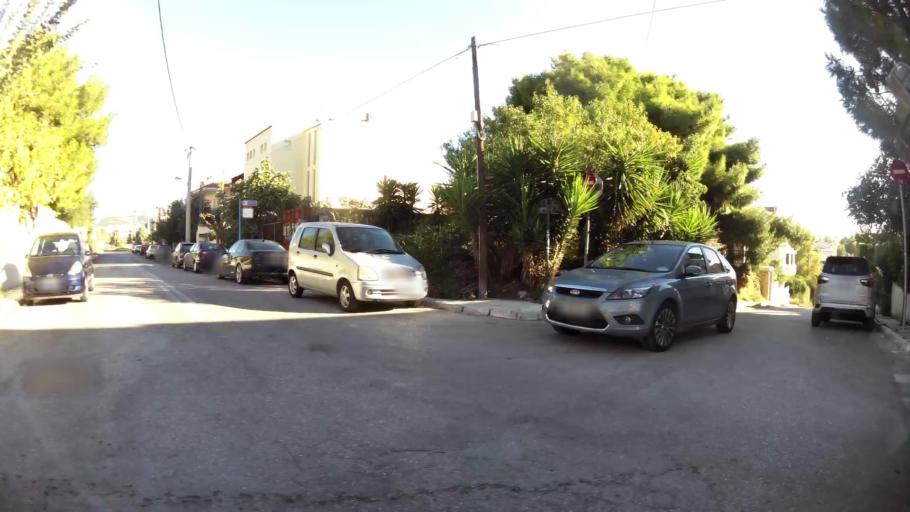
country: GR
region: Attica
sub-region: Nomarchia Anatolikis Attikis
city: Gerakas
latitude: 38.0165
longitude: 23.8501
